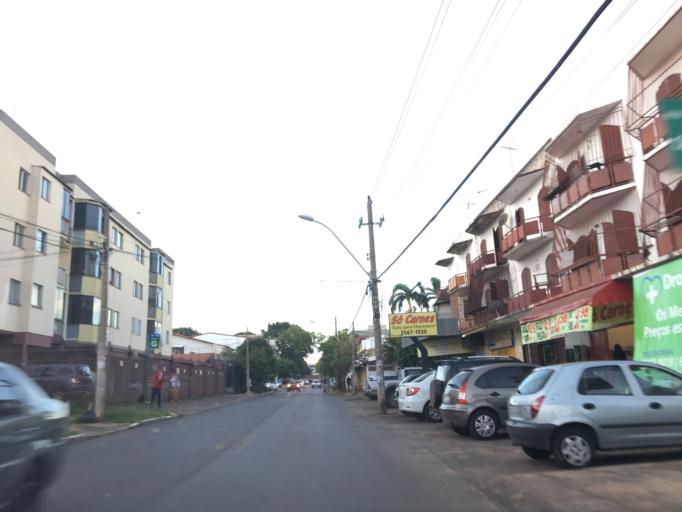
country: BR
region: Federal District
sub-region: Brasilia
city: Brasilia
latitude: -15.8198
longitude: -47.9753
